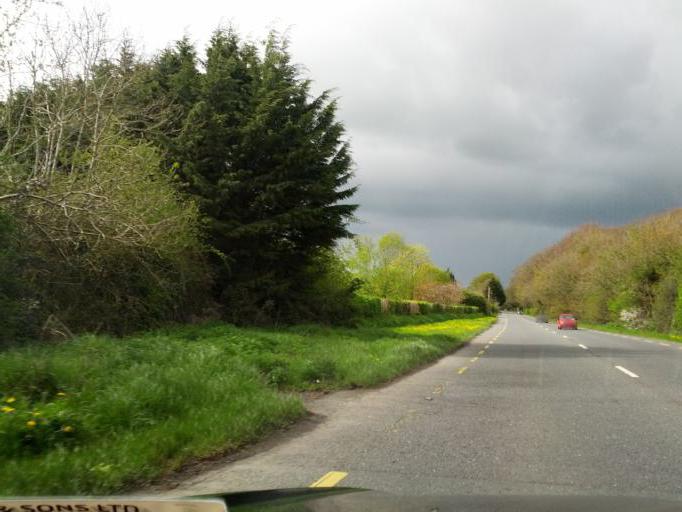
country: IE
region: Leinster
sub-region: An Mhi
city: Dunshaughlin
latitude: 53.5314
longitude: -6.5588
